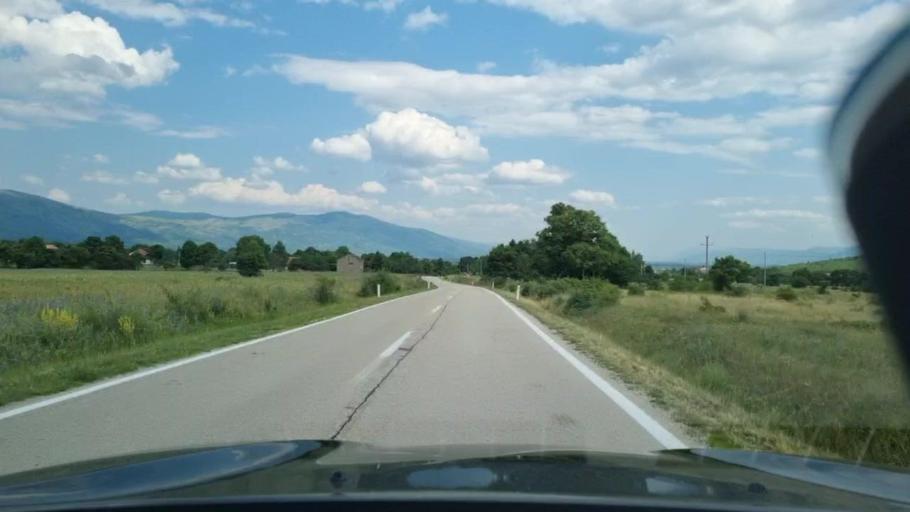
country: BA
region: Federation of Bosnia and Herzegovina
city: Bosansko Grahovo
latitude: 44.0941
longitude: 16.5590
